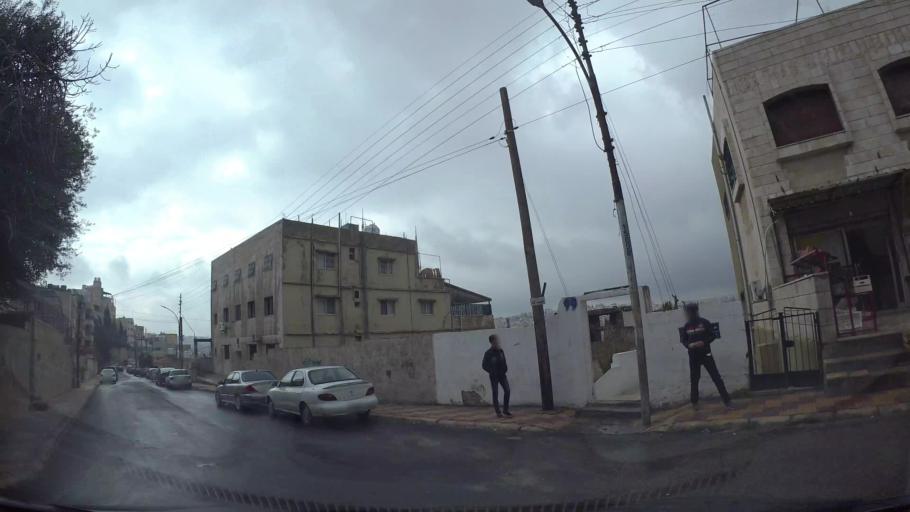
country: JO
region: Amman
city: Amman
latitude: 31.9506
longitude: 35.9153
